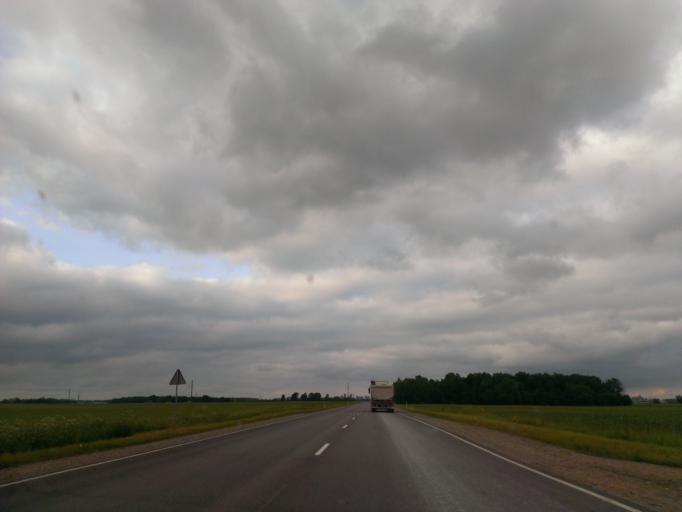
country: LV
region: Saldus Rajons
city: Saldus
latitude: 56.6707
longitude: 22.4277
